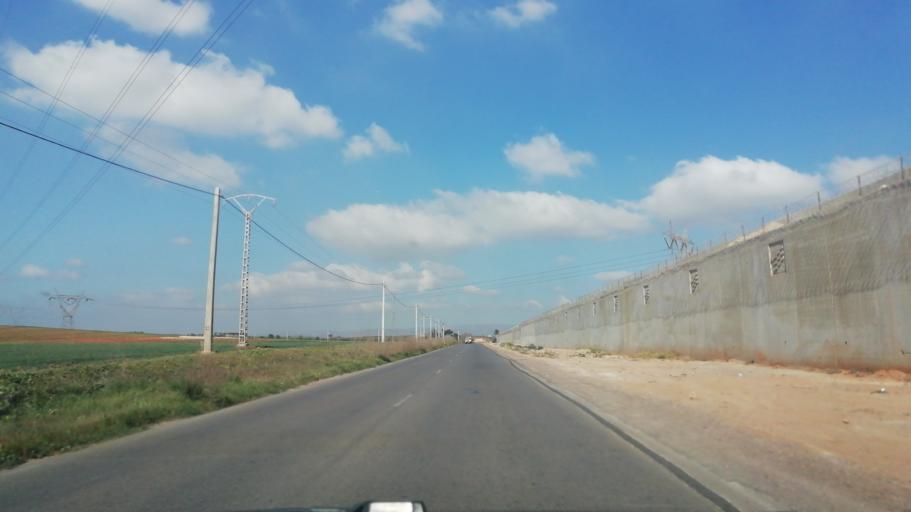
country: DZ
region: Oran
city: Ain el Bya
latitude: 35.7531
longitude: -0.2684
